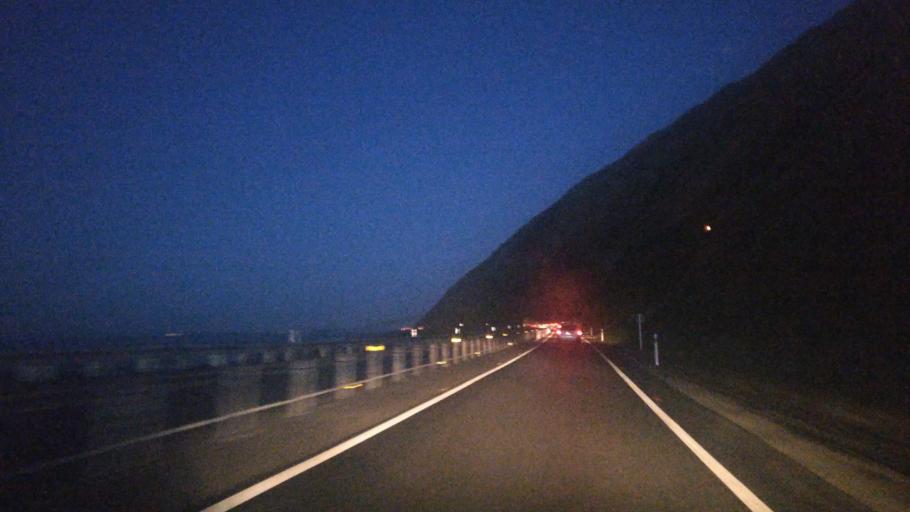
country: NZ
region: Wellington
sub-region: Porirua City
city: Porirua
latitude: -41.0156
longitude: 174.9167
